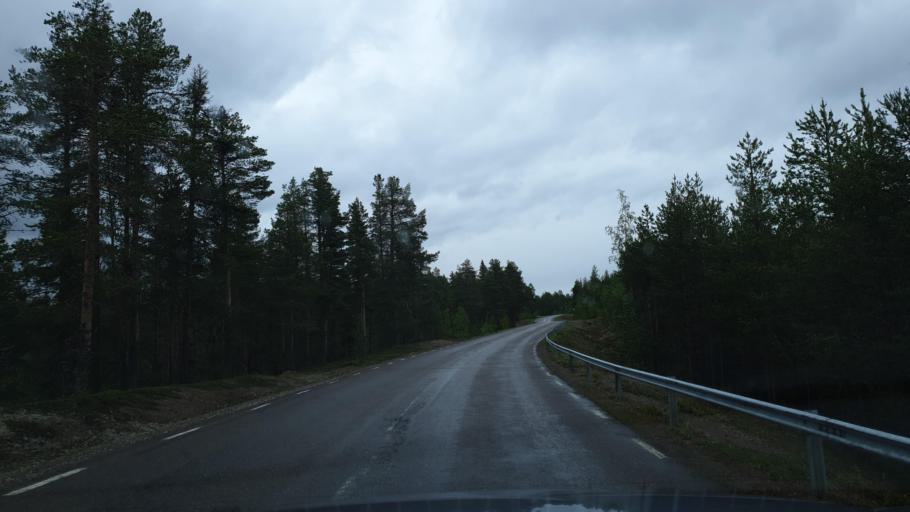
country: SE
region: Norrbotten
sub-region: Kiruna Kommun
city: Kiruna
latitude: 67.8813
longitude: 20.9982
